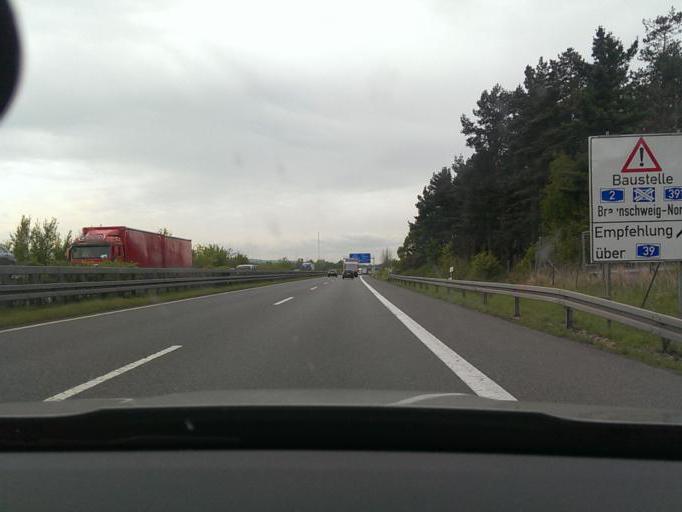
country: DE
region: Lower Saxony
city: Lehre
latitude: 52.3224
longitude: 10.7326
